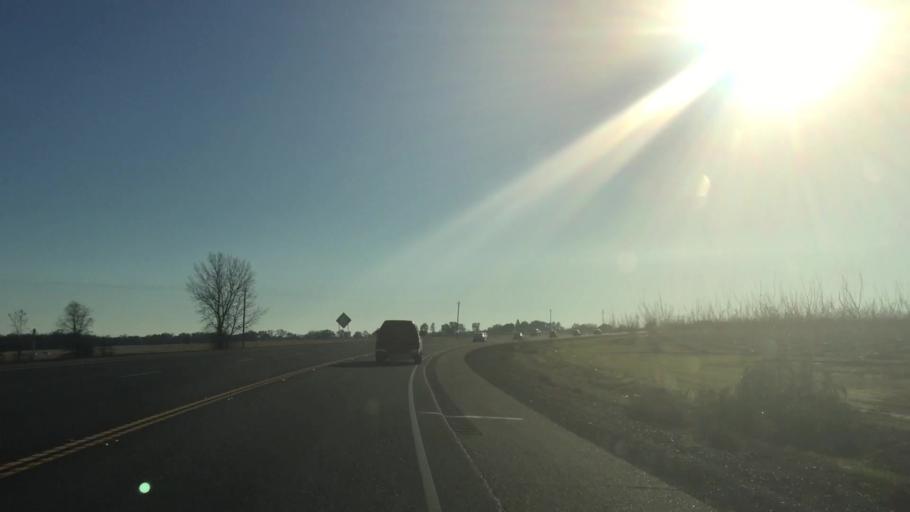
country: US
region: California
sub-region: Butte County
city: Palermo
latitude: 39.3928
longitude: -121.6058
